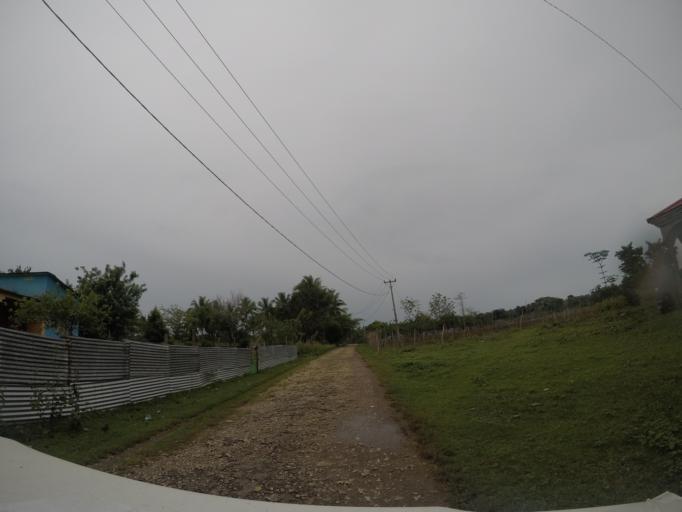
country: TL
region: Lautem
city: Lospalos
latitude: -8.5257
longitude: 127.0054
